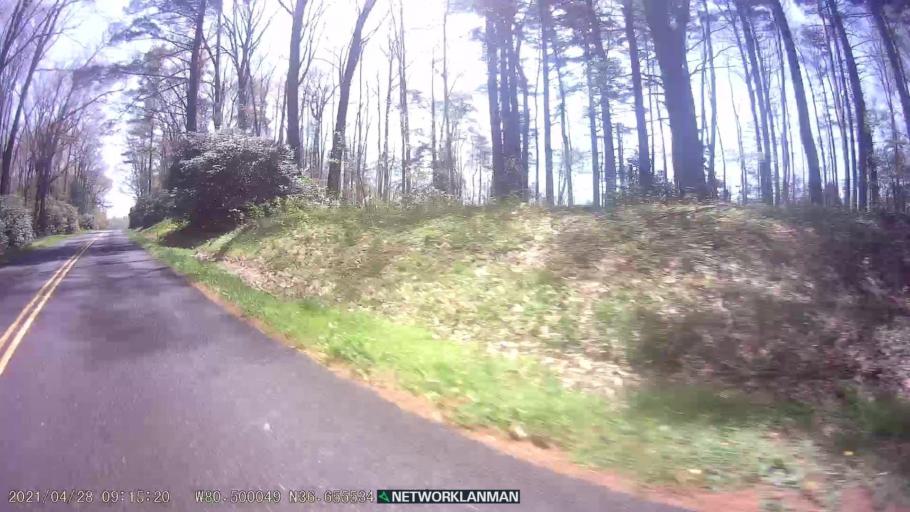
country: US
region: North Carolina
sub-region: Surry County
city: Flat Rock
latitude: 36.6555
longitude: -80.4998
